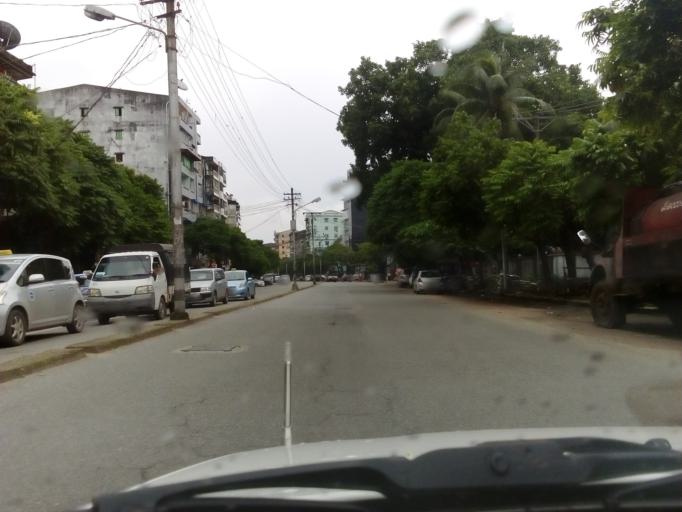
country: MM
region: Yangon
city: Yangon
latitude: 16.8020
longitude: 96.1750
